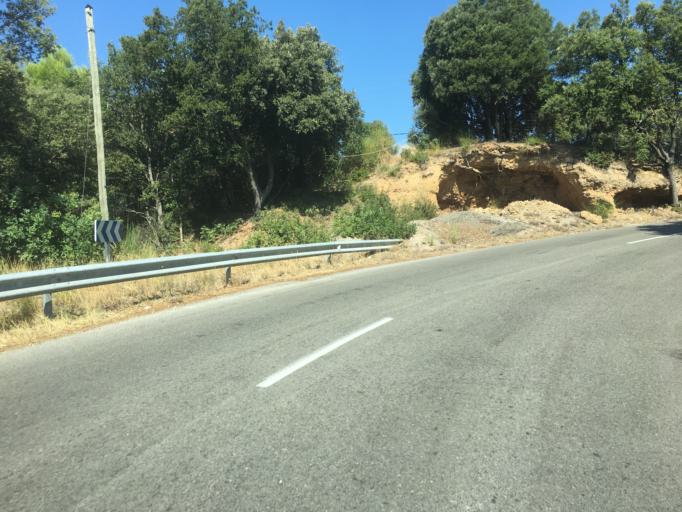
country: FR
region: Provence-Alpes-Cote d'Azur
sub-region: Departement des Alpes-de-Haute-Provence
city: Volx
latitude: 43.8296
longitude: 5.8612
